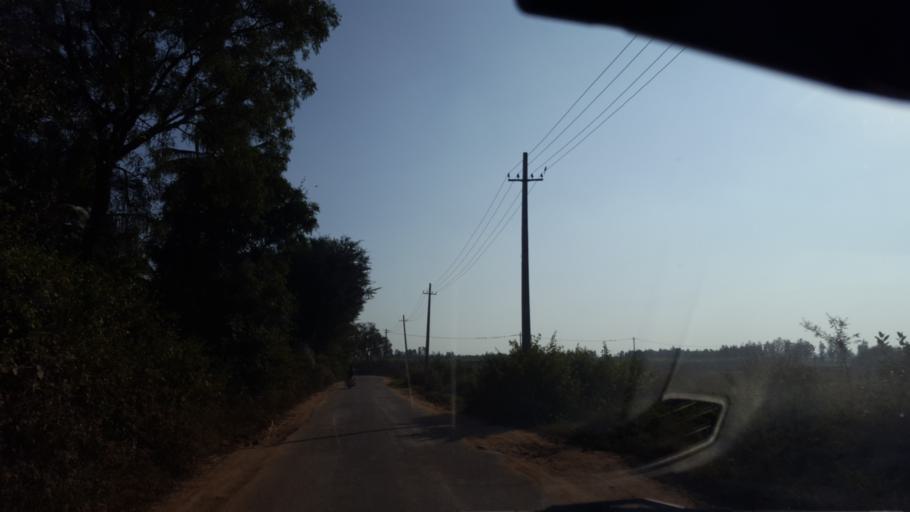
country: IN
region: Karnataka
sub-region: Bangalore Rural
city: Hoskote
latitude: 12.9273
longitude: 77.7567
